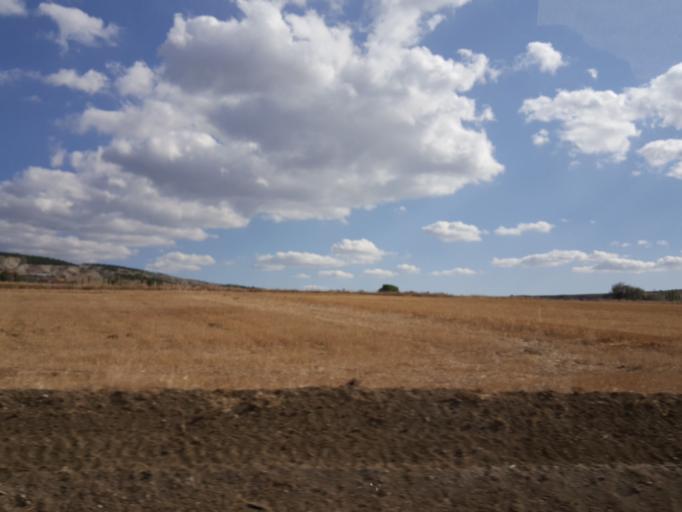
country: TR
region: Tokat
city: Sulusaray
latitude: 39.9877
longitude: 35.9821
